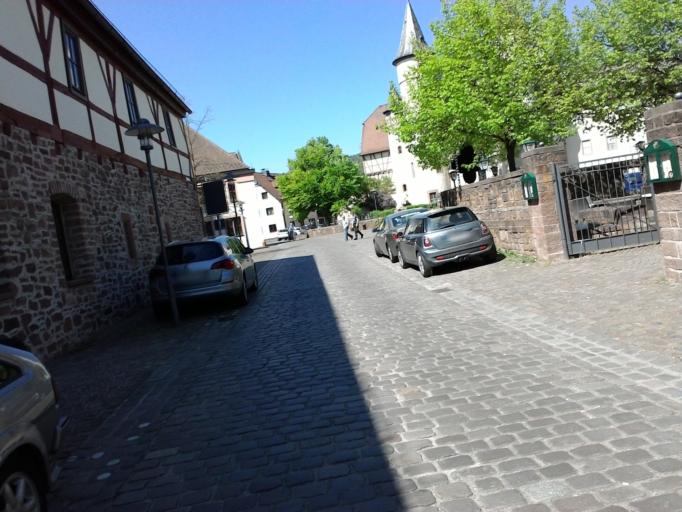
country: DE
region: Bavaria
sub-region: Regierungsbezirk Unterfranken
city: Lohr am Main
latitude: 49.9956
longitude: 9.5739
